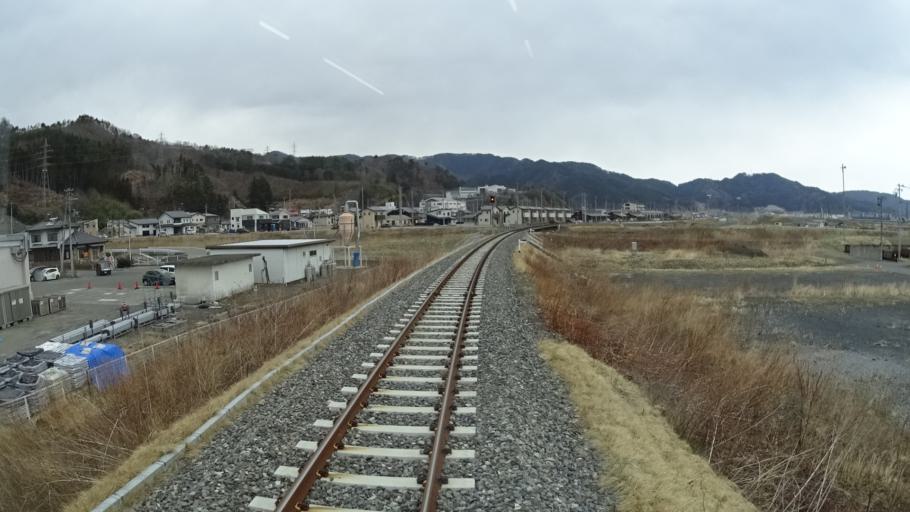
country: JP
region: Iwate
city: Otsuchi
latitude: 39.3546
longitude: 141.8954
